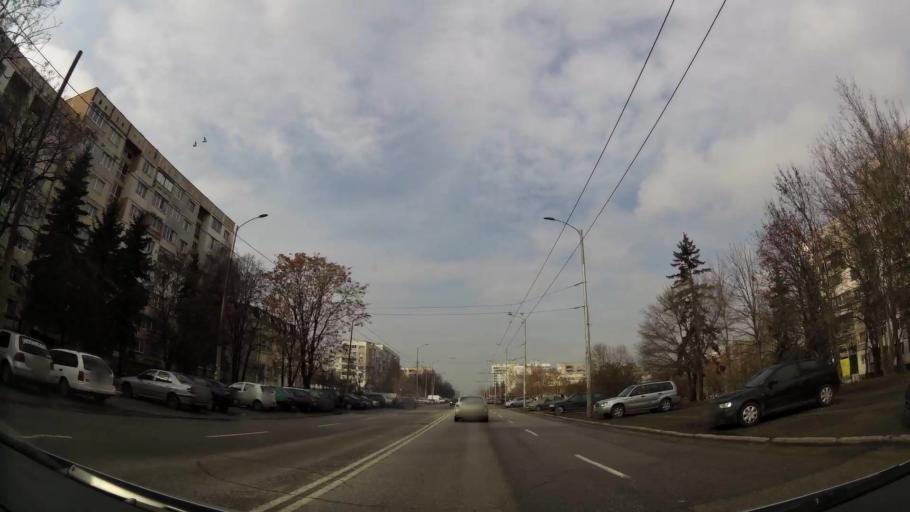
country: BG
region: Sofiya
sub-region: Obshtina Bozhurishte
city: Bozhurishte
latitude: 42.7191
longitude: 23.2454
